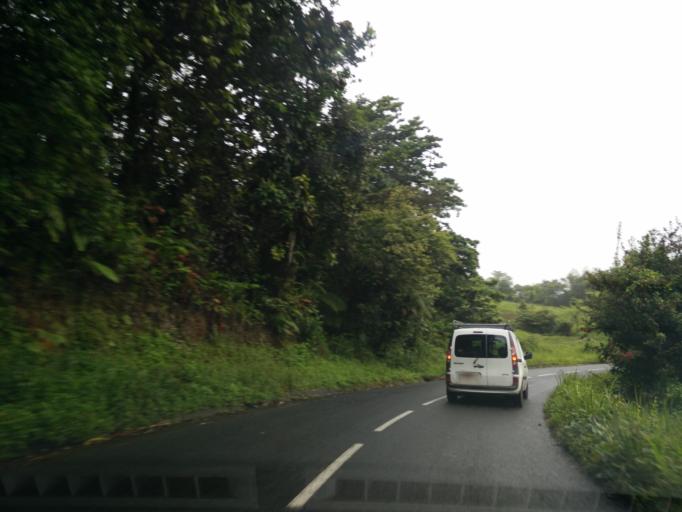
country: MQ
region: Martinique
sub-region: Martinique
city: Le Morne-Rouge
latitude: 14.7208
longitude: -61.0986
